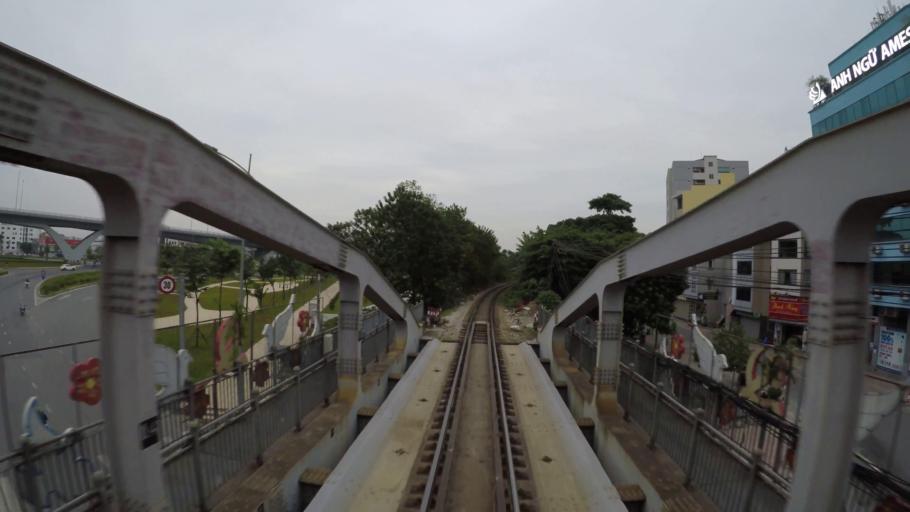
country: VN
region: Ha Noi
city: Trau Quy
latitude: 21.0190
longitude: 105.9409
